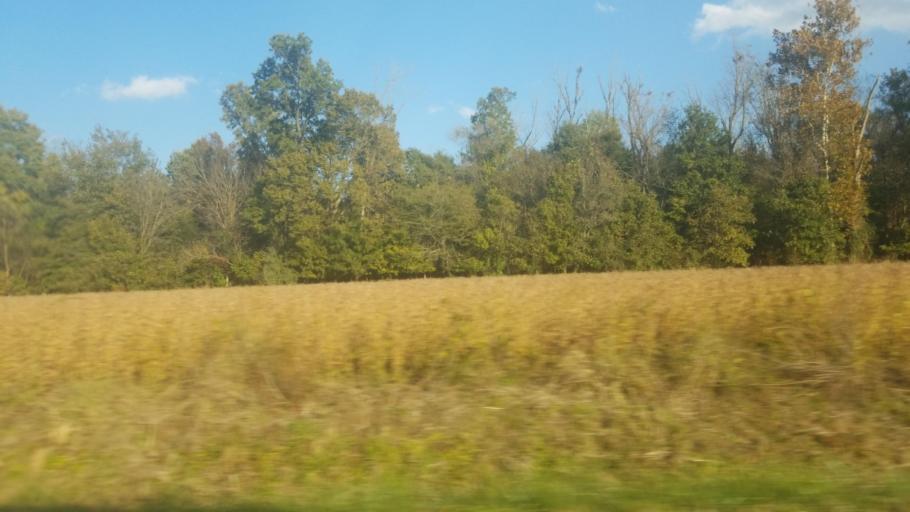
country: US
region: Illinois
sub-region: Saline County
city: Harrisburg
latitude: 37.8212
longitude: -88.6146
